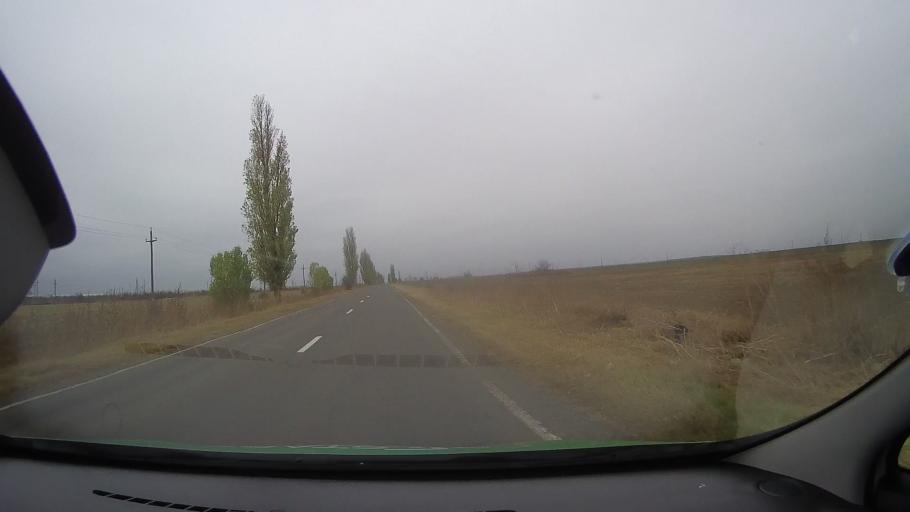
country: RO
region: Ialomita
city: Tandarei
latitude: 44.6581
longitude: 27.6487
